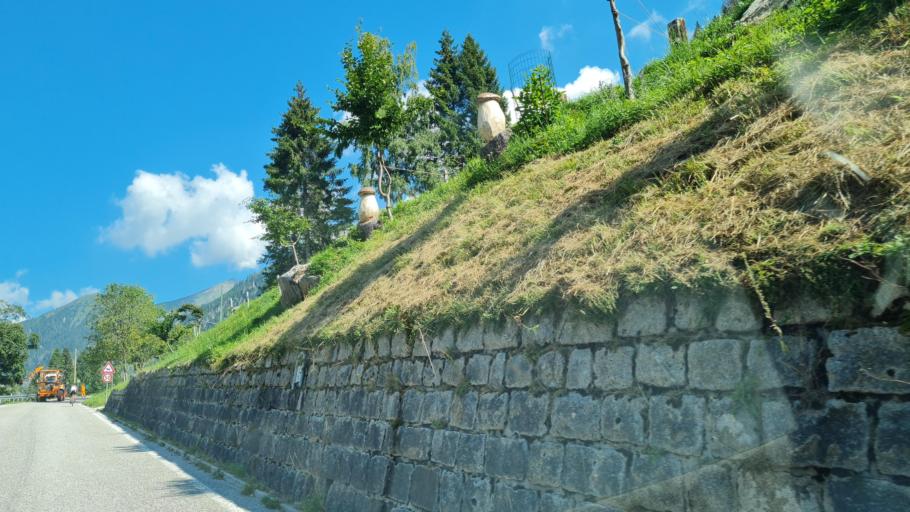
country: IT
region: Trentino-Alto Adige
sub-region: Provincia di Trento
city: Telve di Sopra
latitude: 46.1268
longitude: 11.4805
